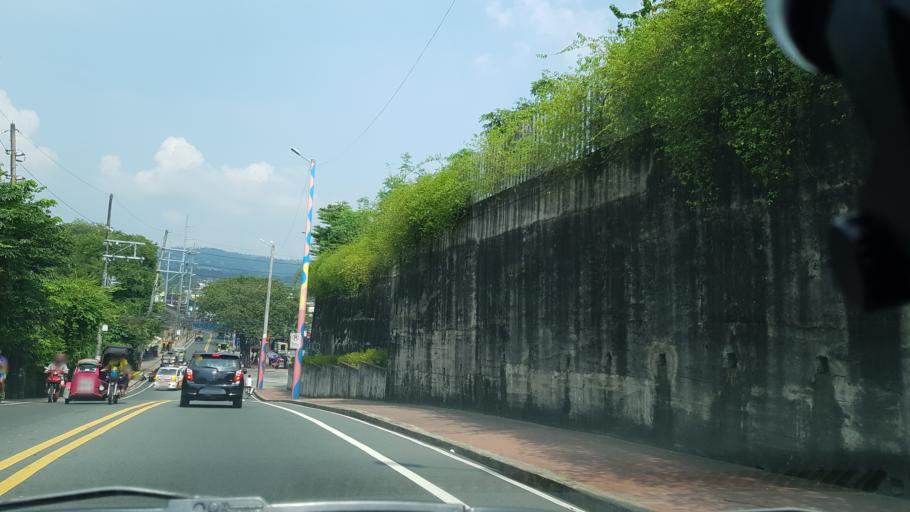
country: PH
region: Calabarzon
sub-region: Province of Rizal
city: San Mateo
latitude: 14.6628
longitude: 121.1235
